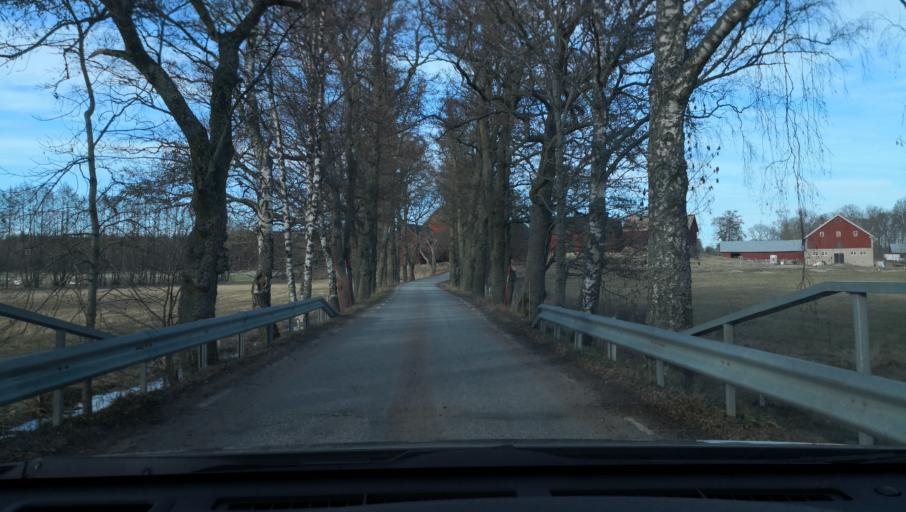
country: SE
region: Uppsala
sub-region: Enkopings Kommun
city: Grillby
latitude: 59.5422
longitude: 17.2023
